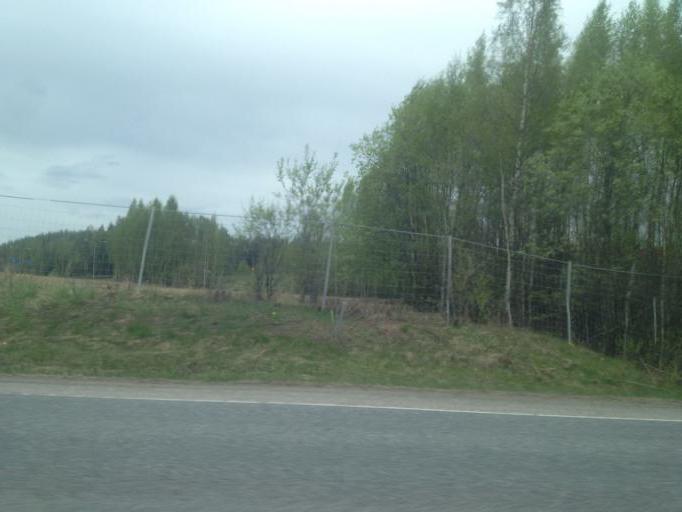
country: FI
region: Uusimaa
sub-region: Helsinki
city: Hyvinge
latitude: 60.5673
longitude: 24.8184
